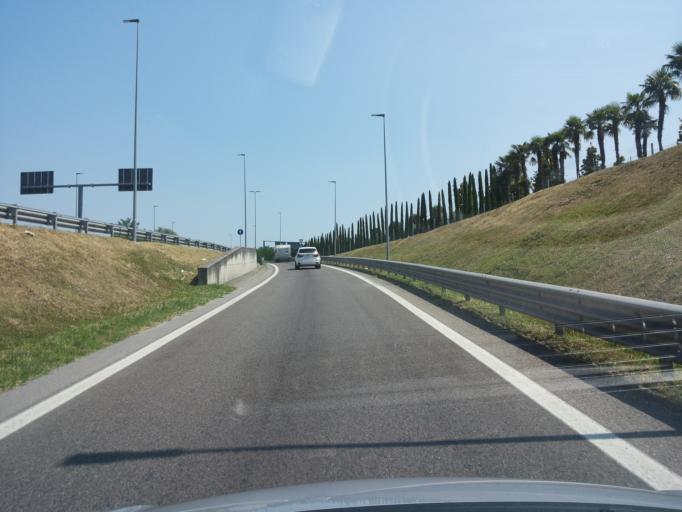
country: IT
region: Veneto
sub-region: Provincia di Verona
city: Cavalcaselle
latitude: 45.4305
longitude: 10.7086
